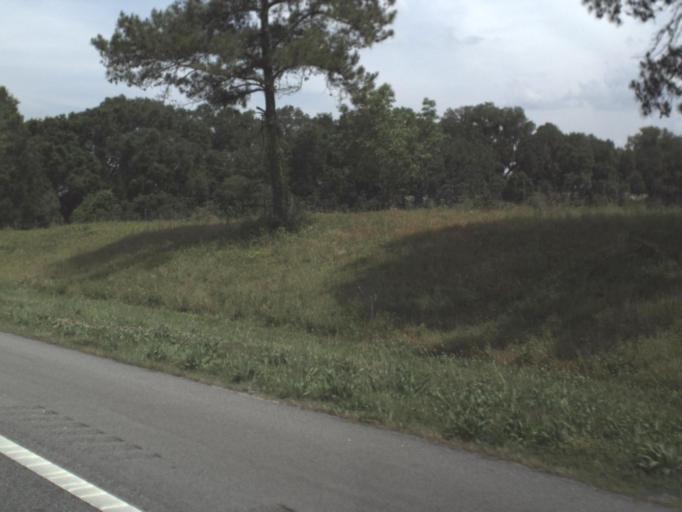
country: US
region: Florida
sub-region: Suwannee County
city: Live Oak
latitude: 30.3516
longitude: -83.0405
